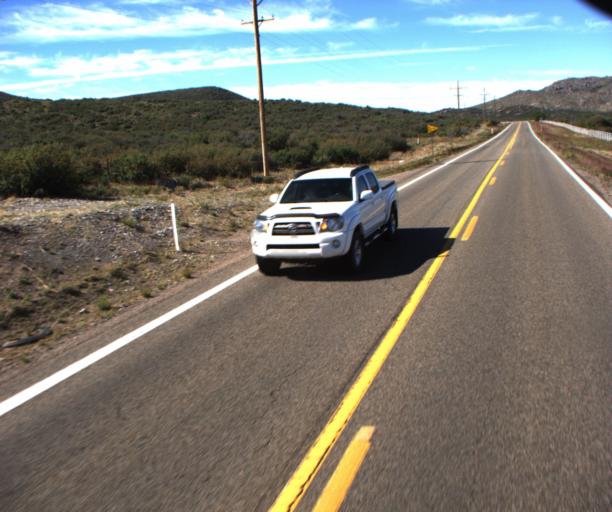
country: US
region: Arizona
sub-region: Yavapai County
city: Congress
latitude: 34.2558
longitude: -112.7326
